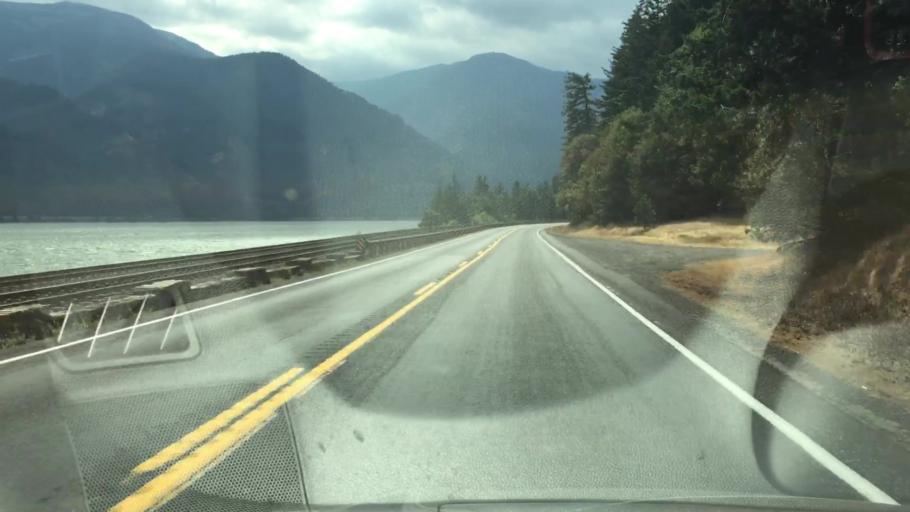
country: US
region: Washington
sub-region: Skamania County
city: Carson
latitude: 45.7066
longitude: -121.6826
